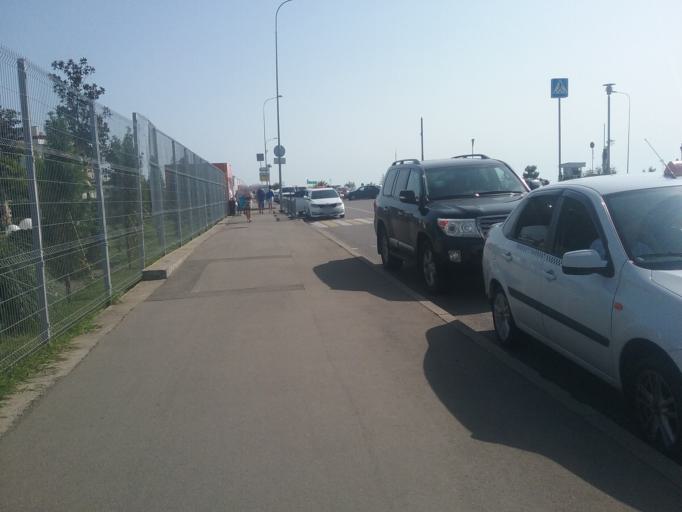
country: RU
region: Krasnodarskiy
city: Adler
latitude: 43.3872
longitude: 39.9913
